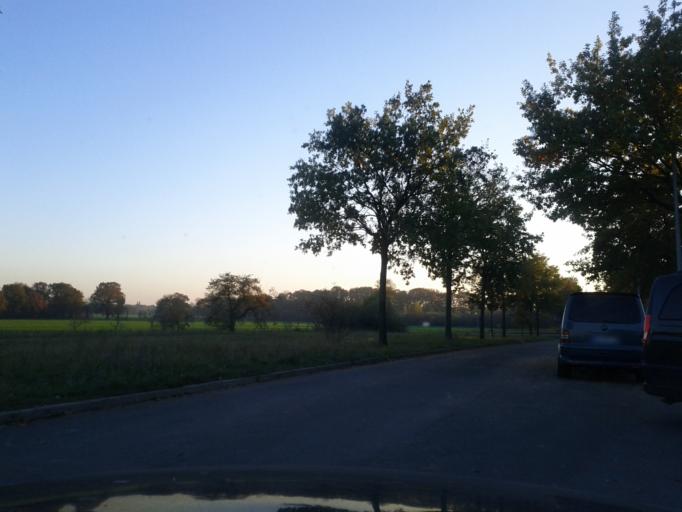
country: DE
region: Brandenburg
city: Schoneiche
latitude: 52.4982
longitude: 13.7060
